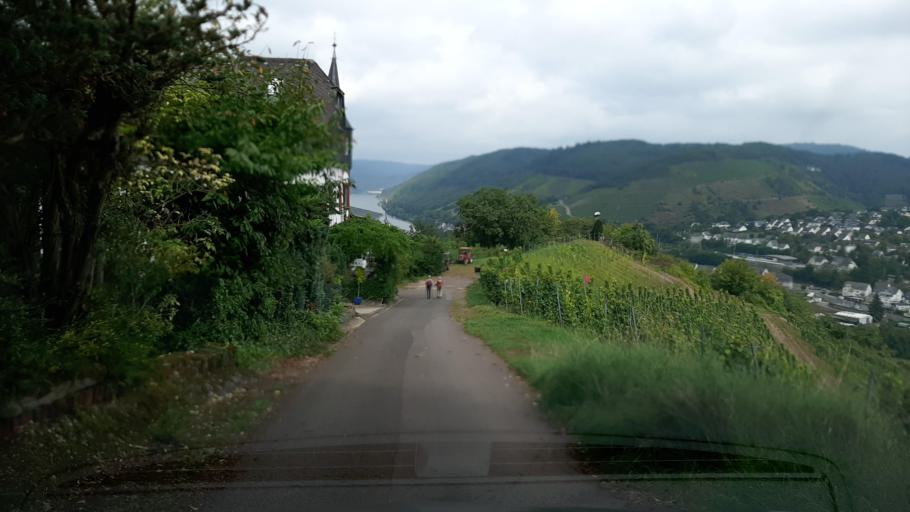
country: DE
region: Rheinland-Pfalz
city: Alf
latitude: 50.0486
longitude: 7.1282
